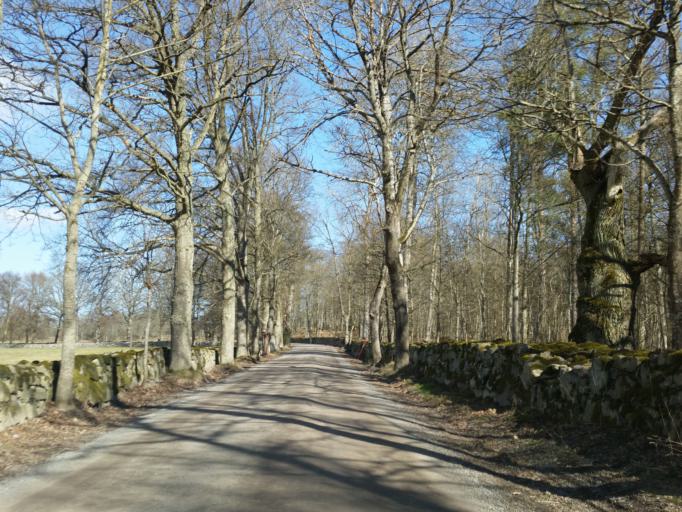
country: SE
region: Kalmar
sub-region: Monsteras Kommun
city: Timmernabben
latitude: 56.9426
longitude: 16.4258
